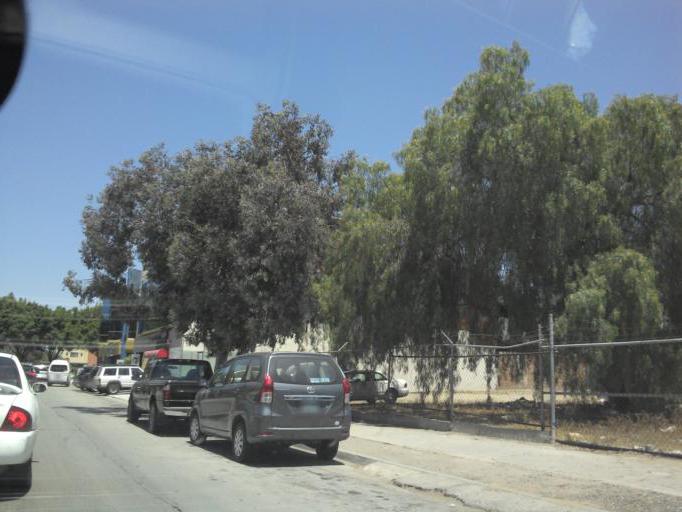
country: MX
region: Baja California
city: Tijuana
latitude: 32.5339
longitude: -117.0218
